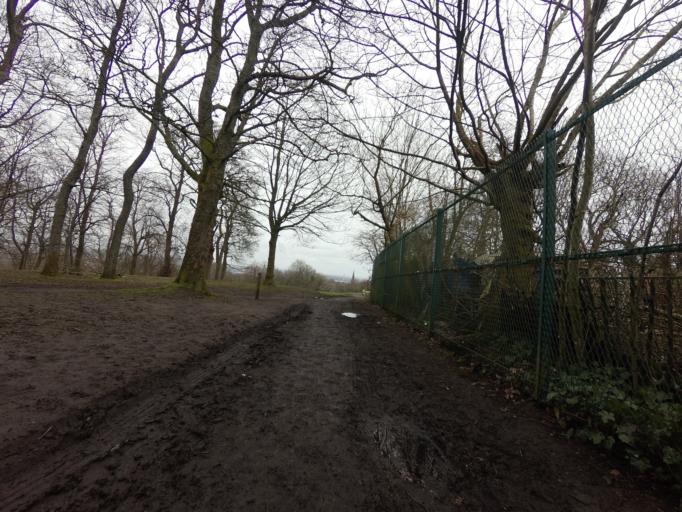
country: GB
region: Scotland
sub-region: East Renfrewshire
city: Giffnock
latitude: 55.8311
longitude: -4.2711
